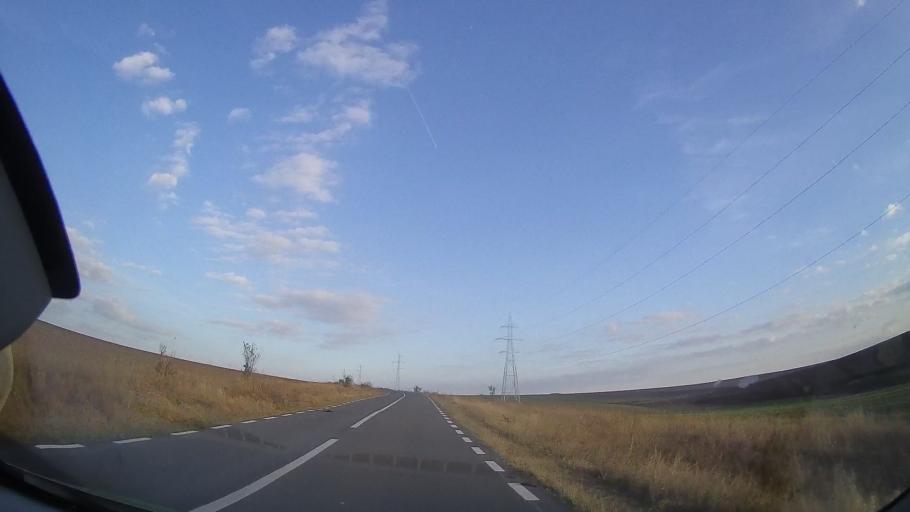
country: RO
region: Constanta
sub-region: Comuna Chirnogeni
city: Plopeni
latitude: 43.9527
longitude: 28.1565
